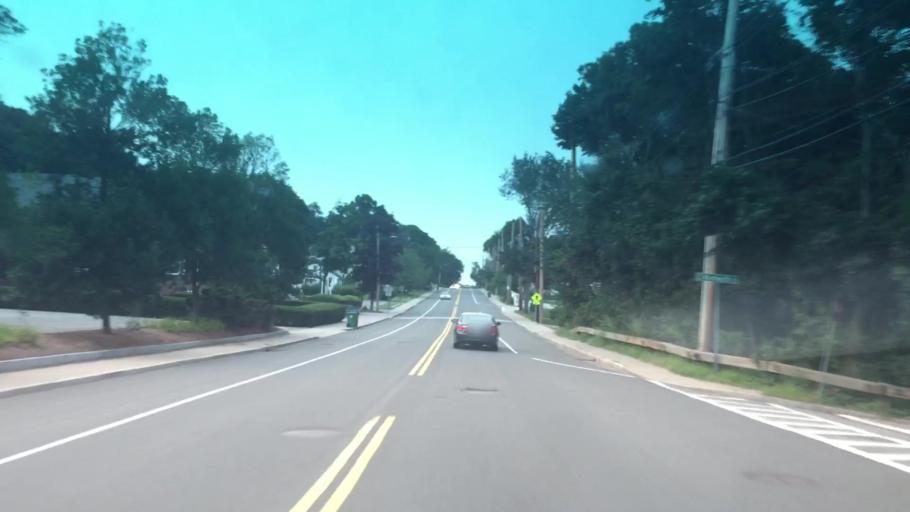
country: US
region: Massachusetts
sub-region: Norfolk County
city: Norwood
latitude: 42.2214
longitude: -71.1876
